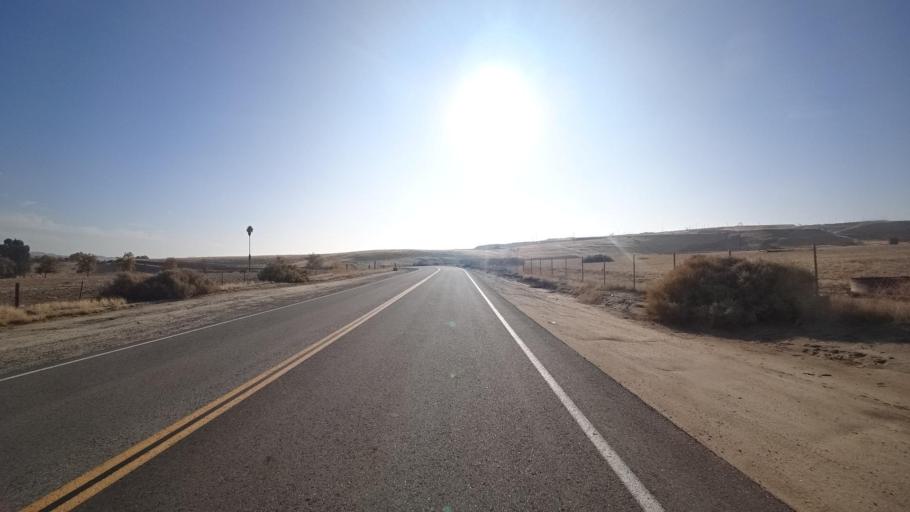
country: US
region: California
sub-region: Kern County
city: Oildale
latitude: 35.4487
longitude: -118.9461
